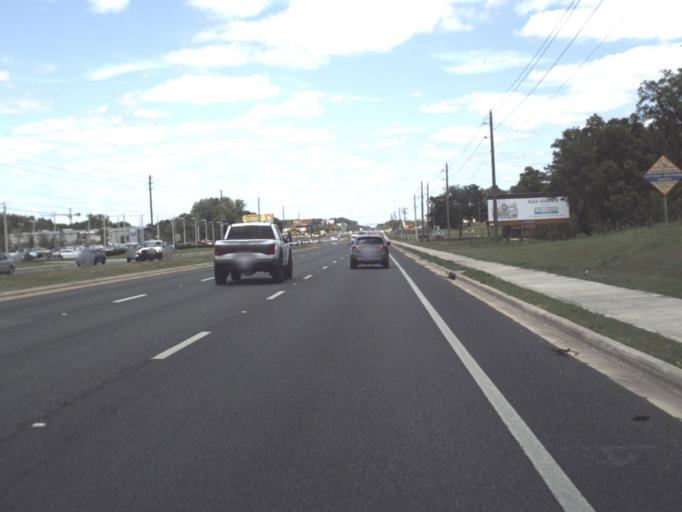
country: US
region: Florida
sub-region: Marion County
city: Ocala
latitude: 29.1298
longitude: -82.2056
